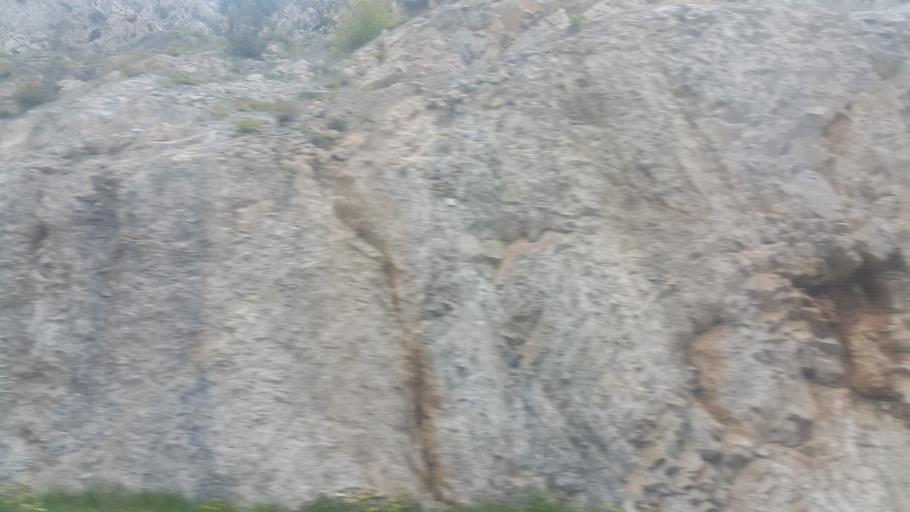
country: TR
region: Adana
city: Pozanti
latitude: 37.4791
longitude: 34.8562
